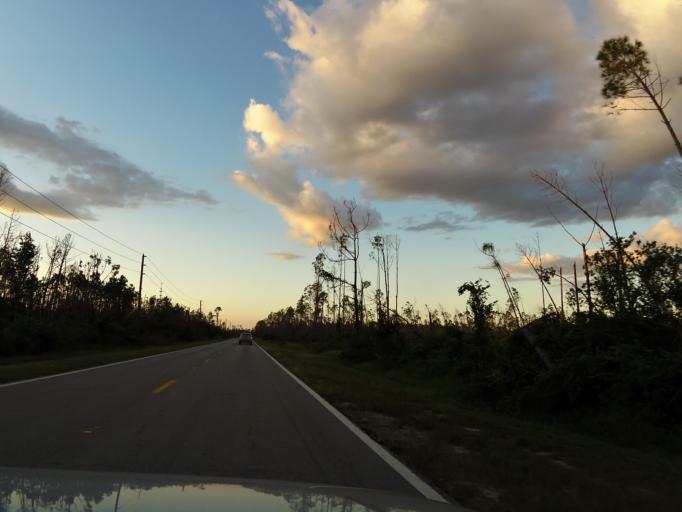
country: US
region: Florida
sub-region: Bay County
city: Mexico Beach
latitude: 29.9346
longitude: -85.3885
